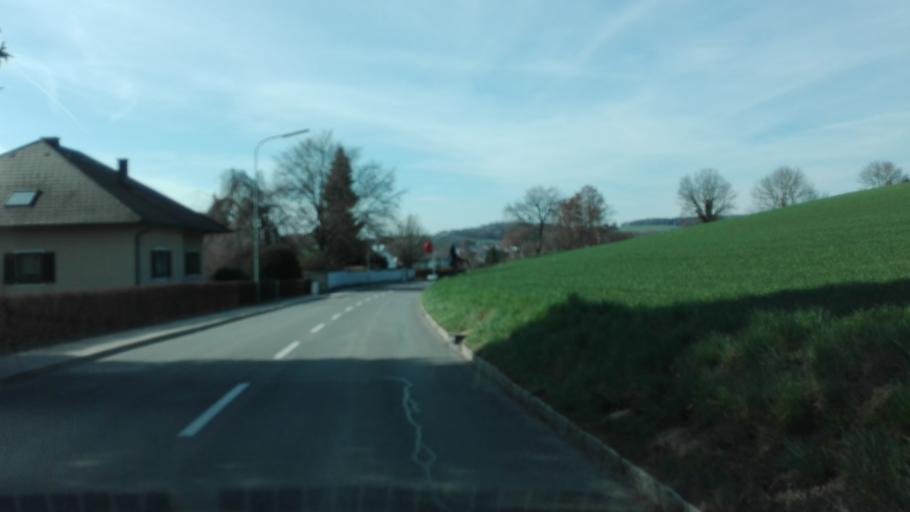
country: AT
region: Upper Austria
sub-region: Politischer Bezirk Perg
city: Perg
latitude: 48.2638
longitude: 14.5876
